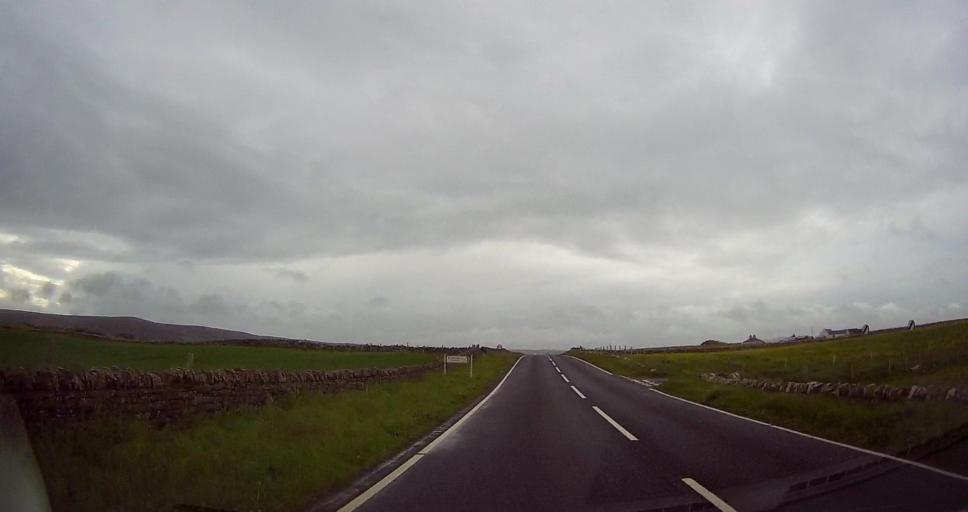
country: GB
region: Scotland
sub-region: Orkney Islands
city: Stromness
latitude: 59.0455
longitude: -3.1931
